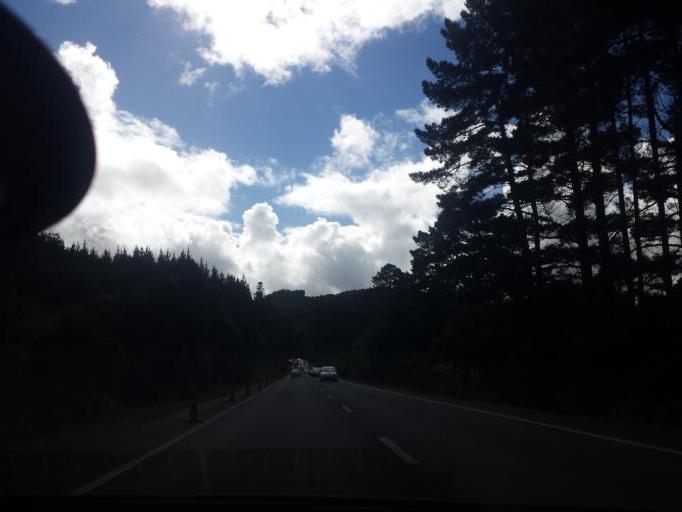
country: NZ
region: Auckland
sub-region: Auckland
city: Warkworth
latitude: -36.5073
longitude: 174.6710
